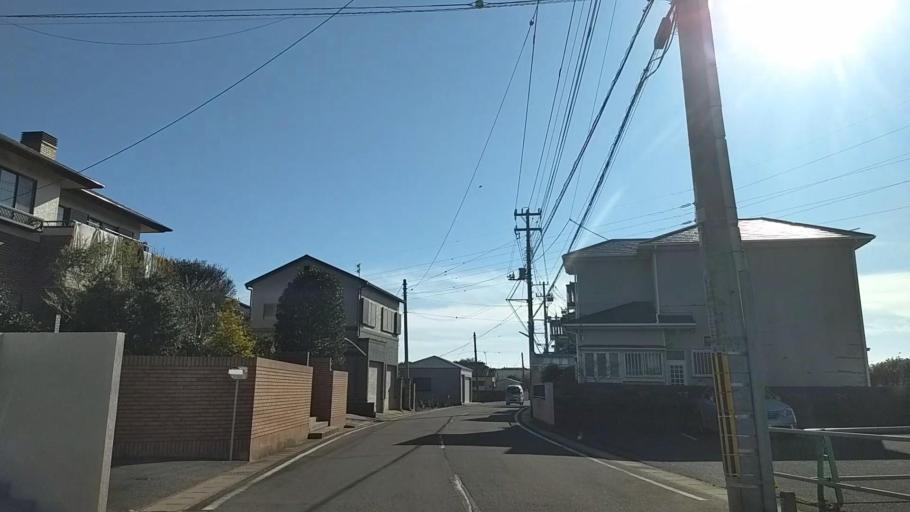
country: JP
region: Chiba
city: Hasaki
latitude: 35.7225
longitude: 140.8431
